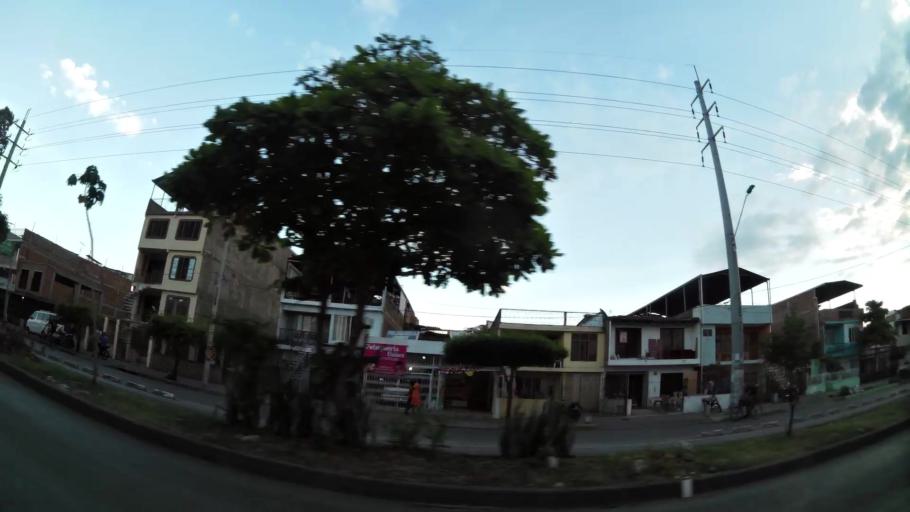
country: CO
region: Valle del Cauca
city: Cali
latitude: 3.4461
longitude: -76.4849
